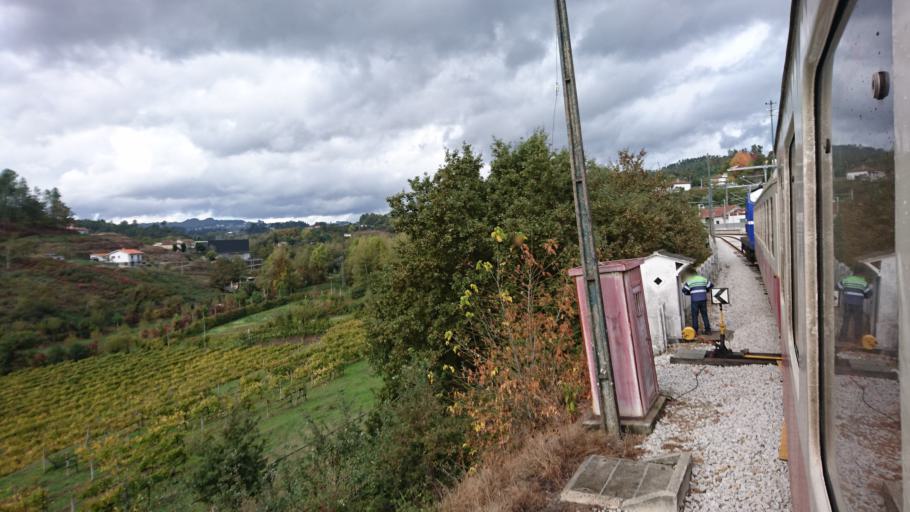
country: PT
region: Porto
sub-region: Marco de Canaveses
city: Marco de Canavezes
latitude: 41.2147
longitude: -8.1542
